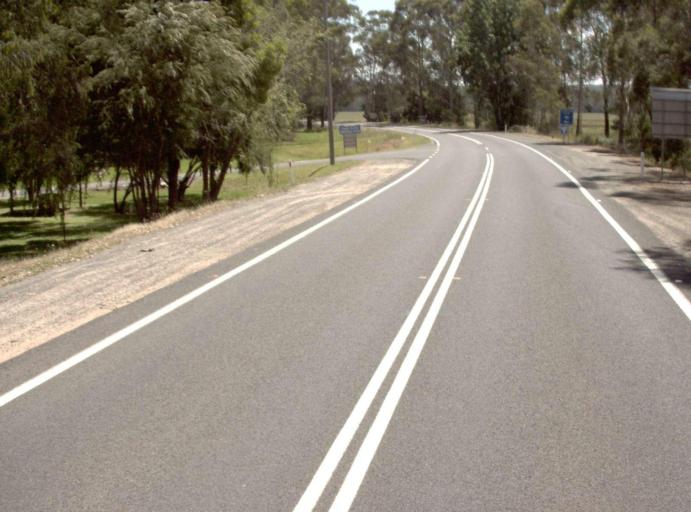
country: AU
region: New South Wales
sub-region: Bombala
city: Bombala
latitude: -37.5663
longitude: 149.1468
